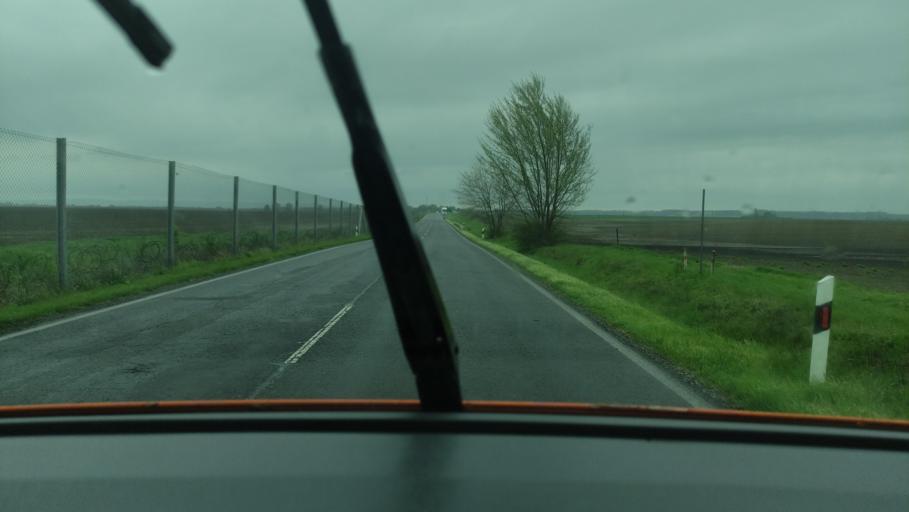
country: HU
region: Baranya
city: Mohacs
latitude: 45.9169
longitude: 18.6594
